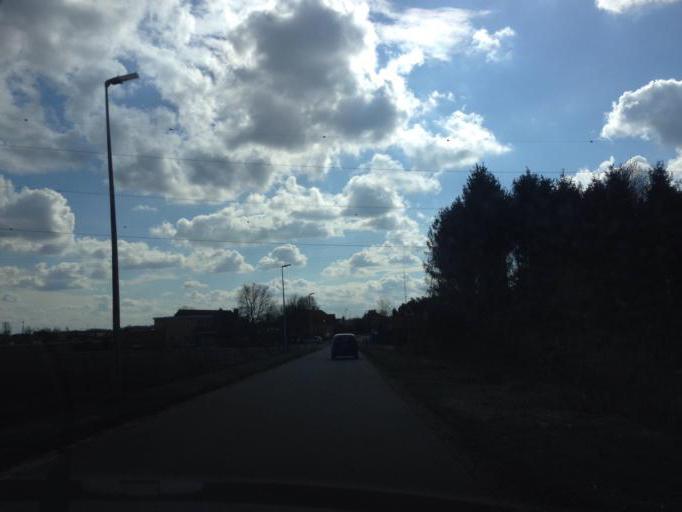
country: BE
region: Flanders
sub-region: Provincie Limburg
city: Bree
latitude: 51.1614
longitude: 5.6075
